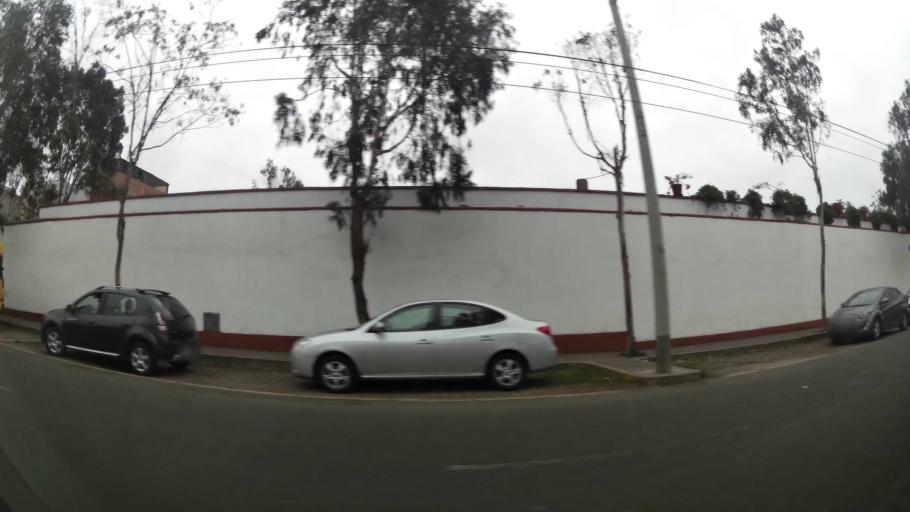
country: PE
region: Lima
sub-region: Lima
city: San Isidro
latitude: -12.0721
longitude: -77.0707
